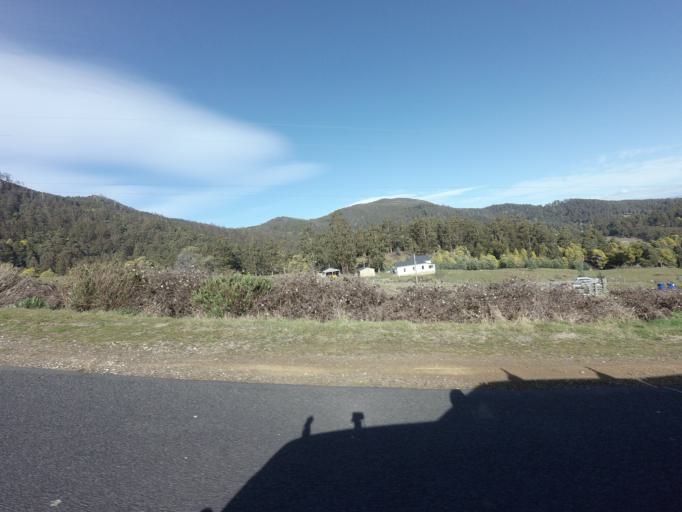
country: AU
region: Tasmania
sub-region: Kingborough
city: Kettering
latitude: -43.1703
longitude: 147.1709
